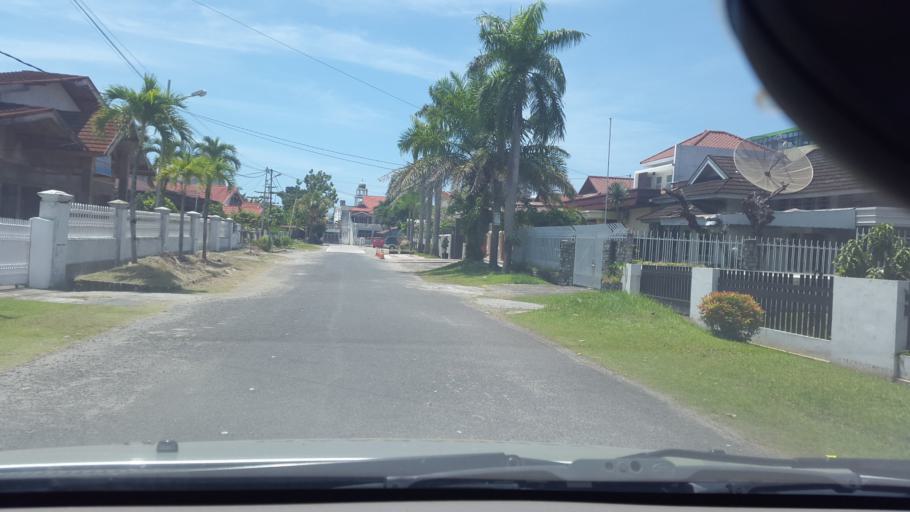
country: ID
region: West Sumatra
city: Padang
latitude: -0.9277
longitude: 100.3539
